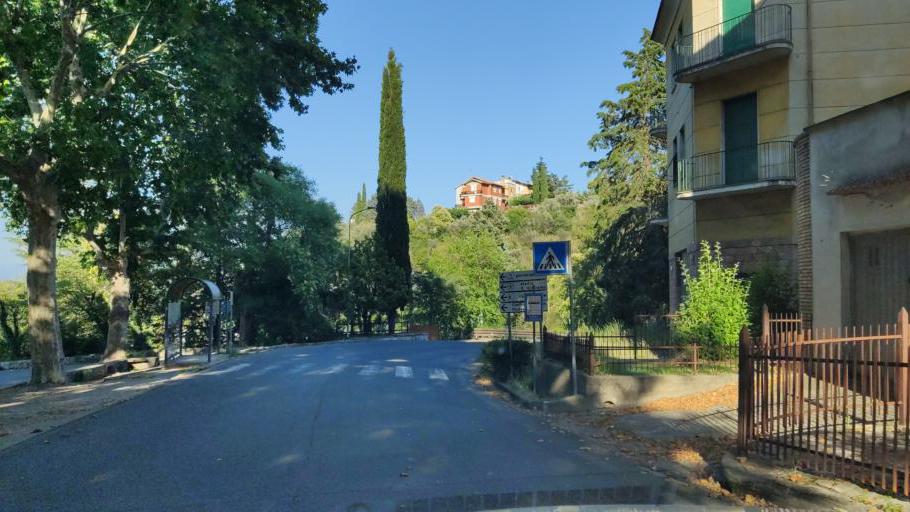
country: IT
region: Umbria
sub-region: Provincia di Terni
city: Narni
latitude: 42.5166
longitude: 12.5236
